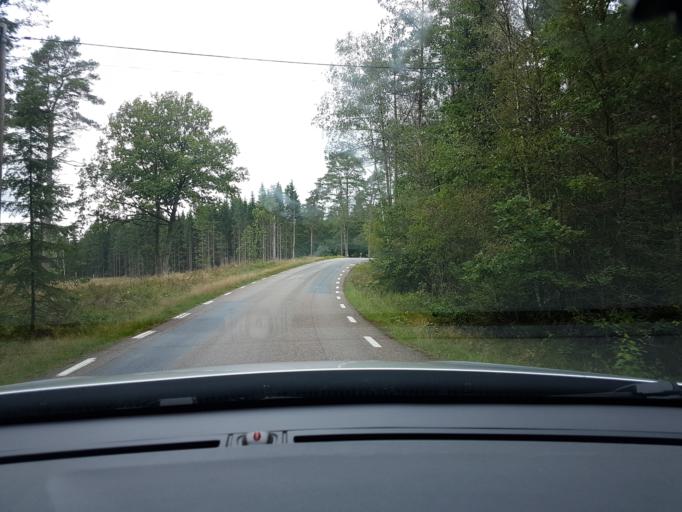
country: SE
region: Vaestra Goetaland
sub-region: Ale Kommun
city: Alvangen
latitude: 57.9024
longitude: 12.1794
